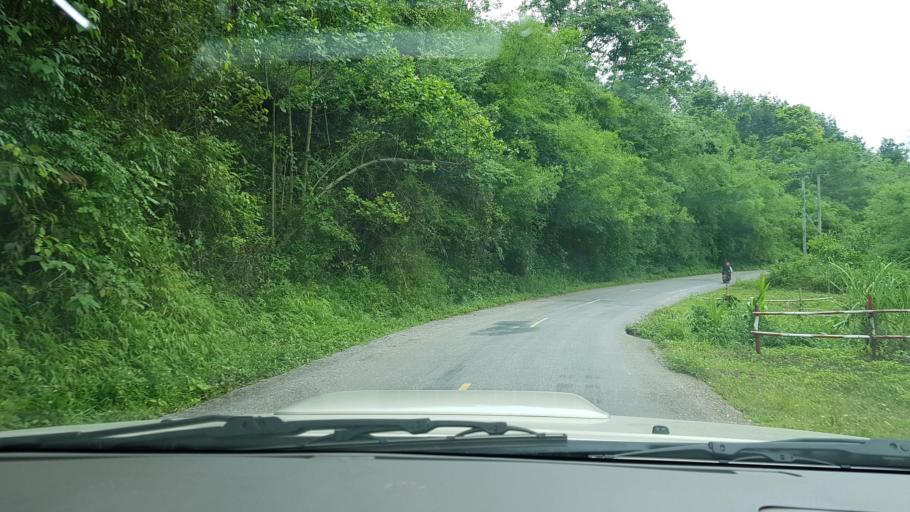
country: LA
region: Oudomxai
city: Muang Xay
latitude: 20.7697
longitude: 102.0578
